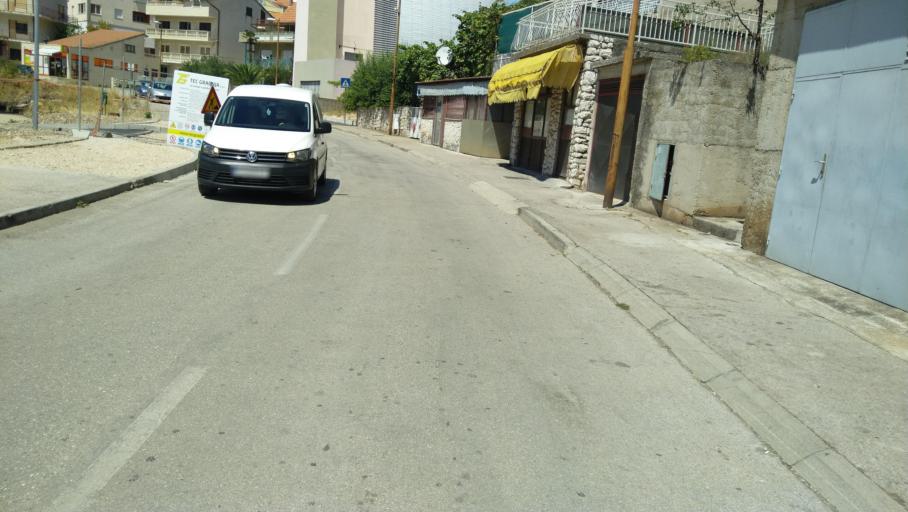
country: HR
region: Sibensko-Kniniska
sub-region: Grad Sibenik
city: Sibenik
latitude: 43.7254
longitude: 15.9120
